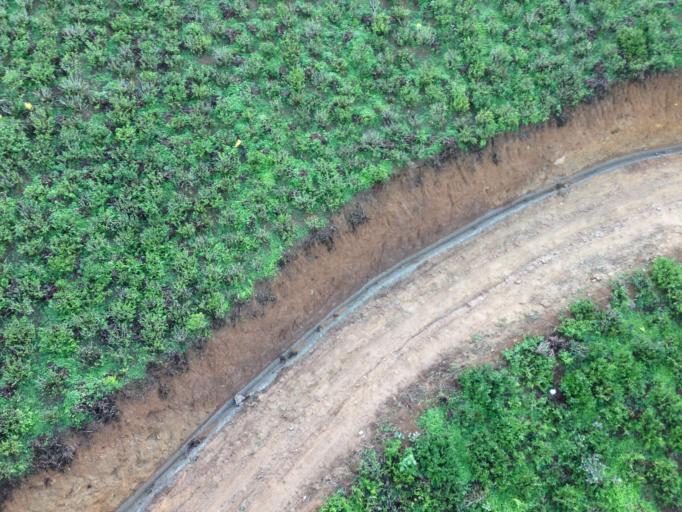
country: IN
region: West Bengal
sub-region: Darjiling
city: Darjiling
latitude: 27.0718
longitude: 88.2547
